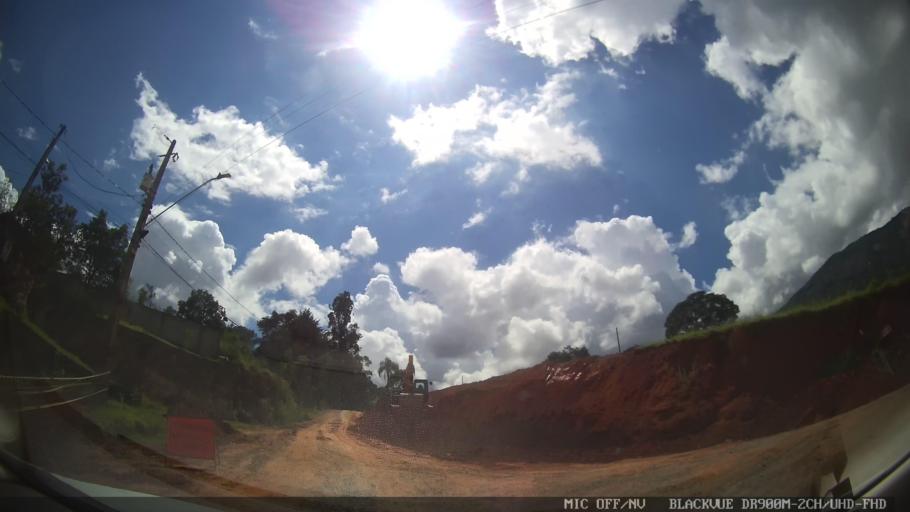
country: BR
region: Minas Gerais
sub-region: Extrema
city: Extrema
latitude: -22.8694
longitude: -46.3396
